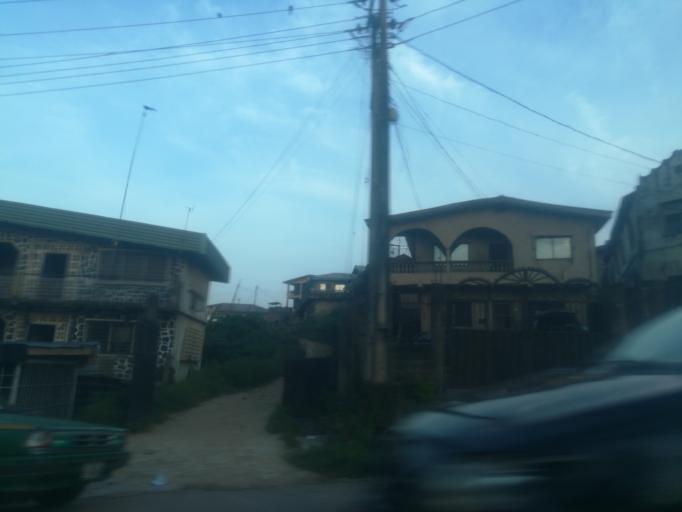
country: NG
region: Ogun
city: Abeokuta
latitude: 7.1463
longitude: 3.3387
